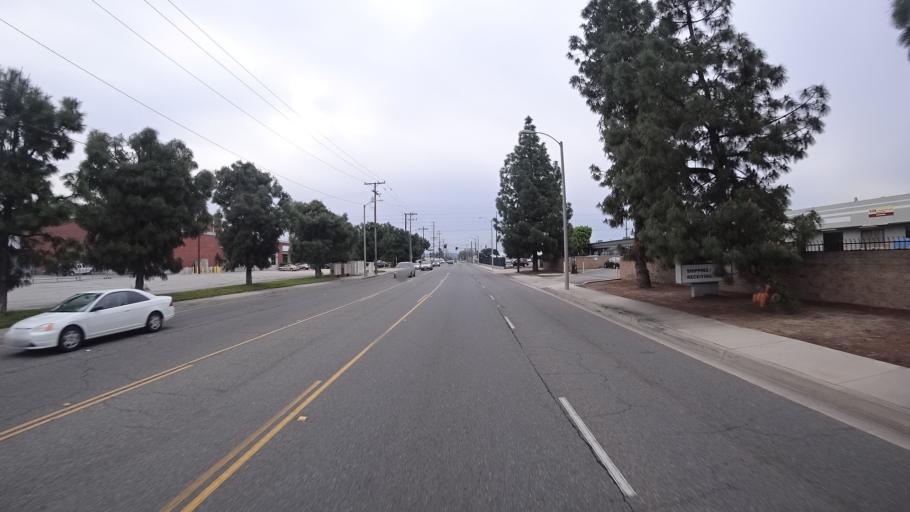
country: US
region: California
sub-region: Los Angeles County
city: Avocado Heights
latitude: 34.0582
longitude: -117.9930
